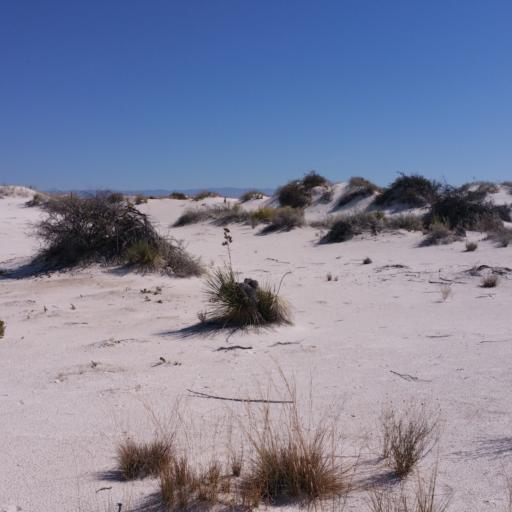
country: US
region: New Mexico
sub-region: Otero County
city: Holloman Air Force Base
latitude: 32.7946
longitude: -106.2390
